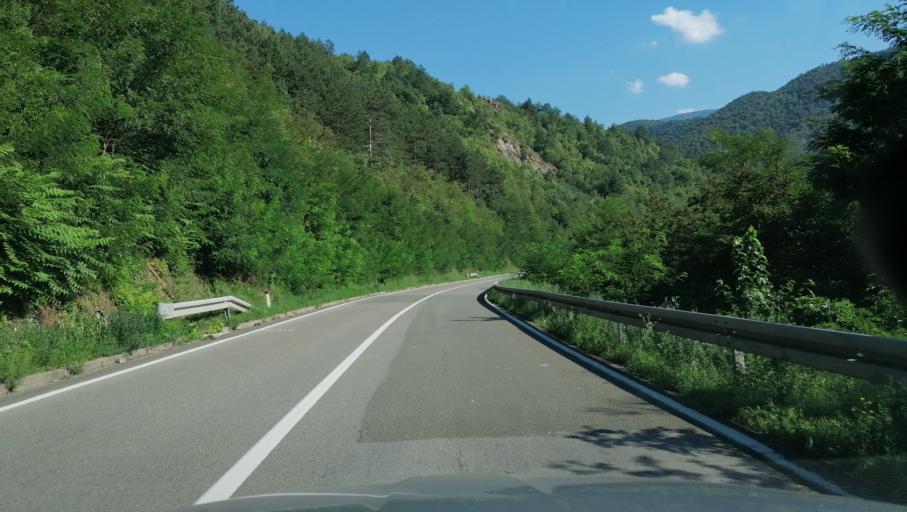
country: RS
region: Central Serbia
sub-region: Raski Okrug
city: Kraljevo
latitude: 43.6646
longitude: 20.5811
